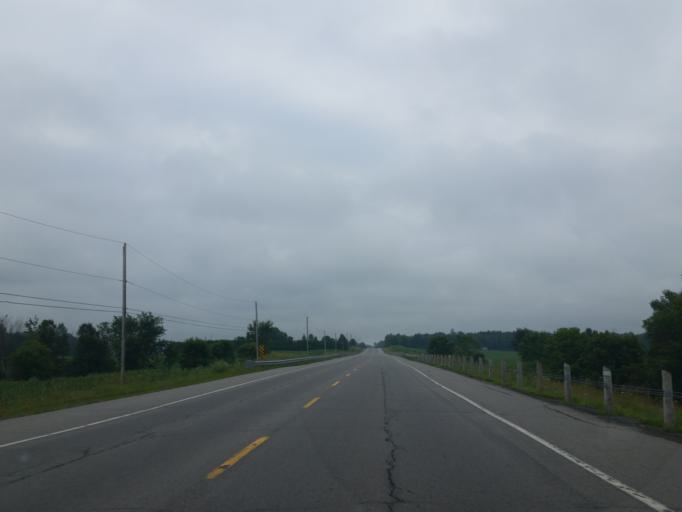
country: CA
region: Ontario
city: Clarence-Rockland
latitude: 45.3988
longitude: -75.3953
